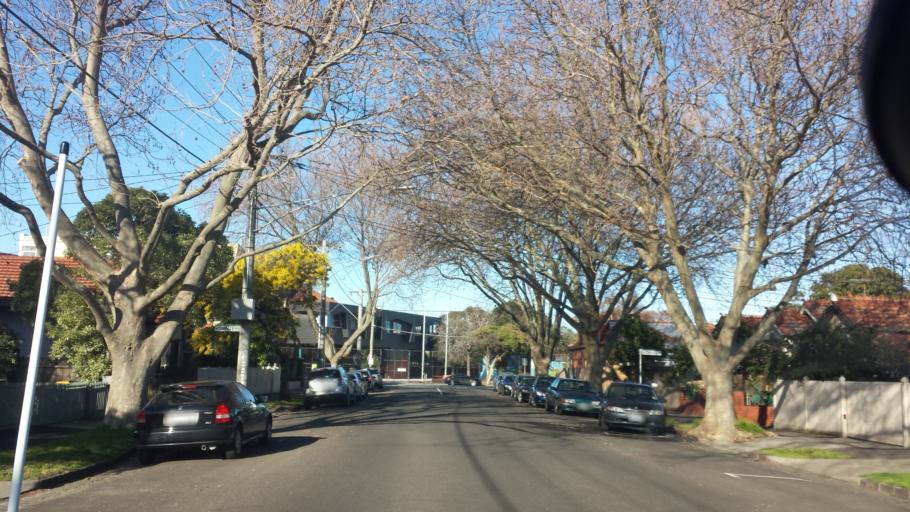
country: AU
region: Victoria
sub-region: Port Phillip
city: Elwood
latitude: -37.8813
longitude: 144.9813
